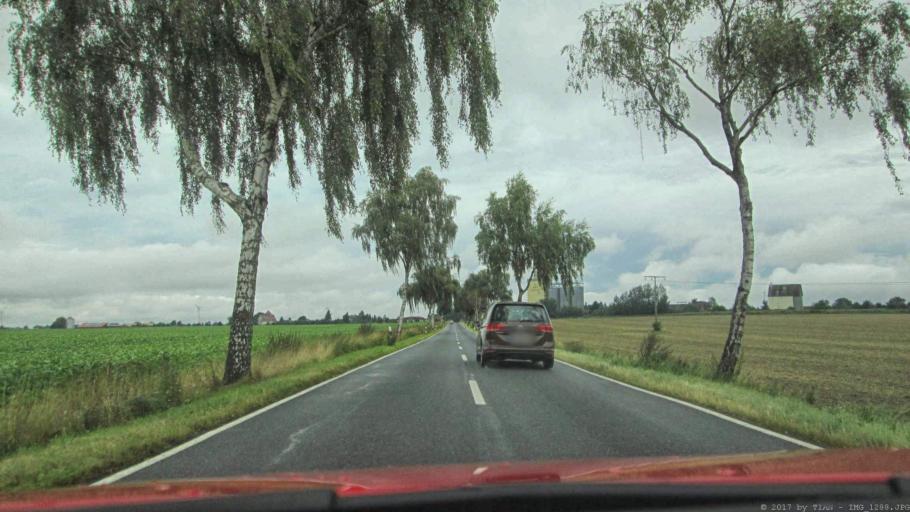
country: DE
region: Lower Saxony
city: Wittingen
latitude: 52.6877
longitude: 10.8072
